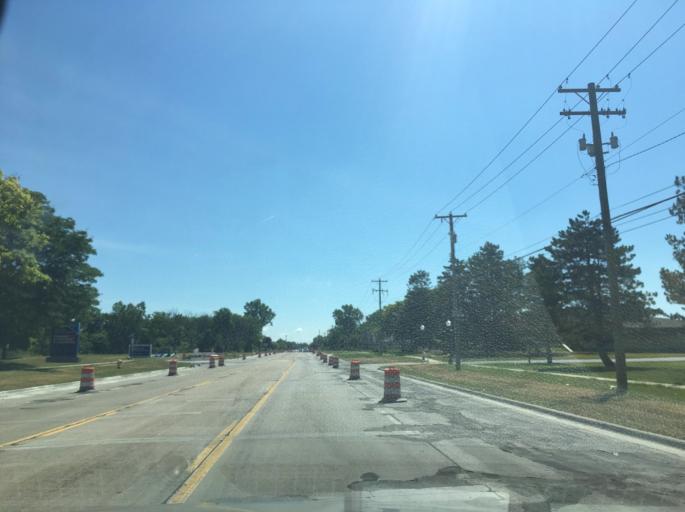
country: US
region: Michigan
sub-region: Macomb County
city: Clinton
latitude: 42.6128
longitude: -82.9591
